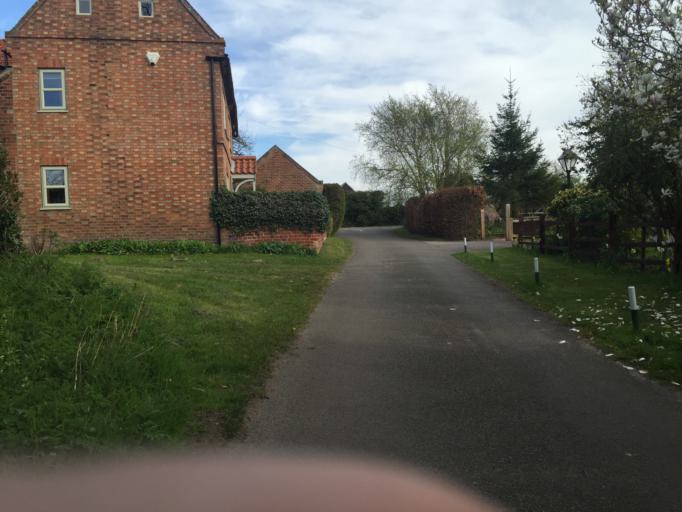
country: GB
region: England
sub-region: Lincolnshire
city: Skellingthorpe
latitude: 53.1256
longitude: -0.6425
